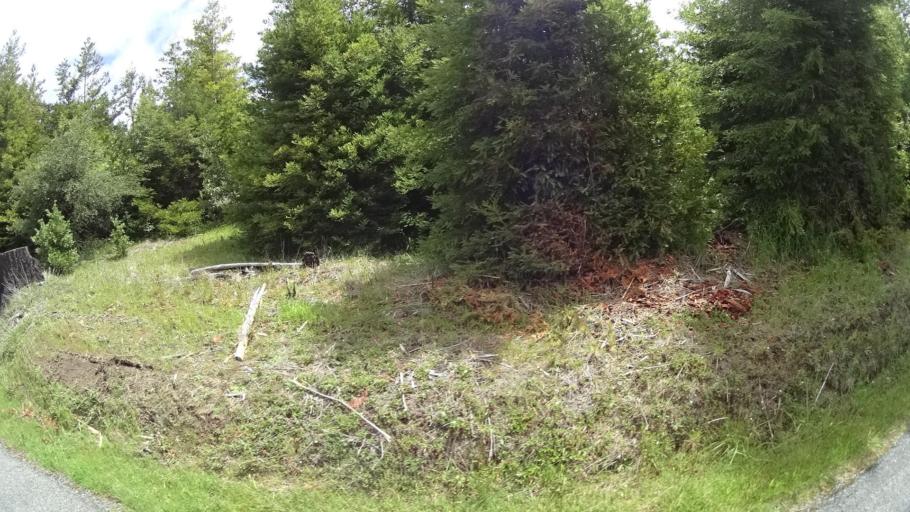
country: US
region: California
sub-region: Humboldt County
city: Blue Lake
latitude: 40.7871
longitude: -123.9658
